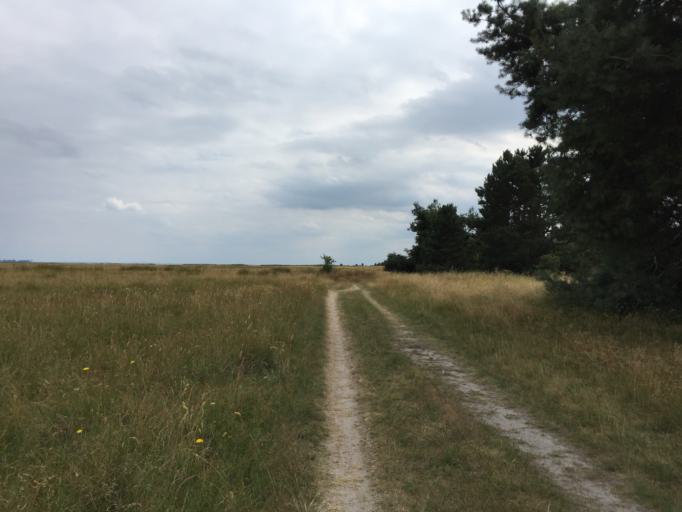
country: DE
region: Mecklenburg-Vorpommern
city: Hiddensee
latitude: 54.5038
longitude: 13.0730
